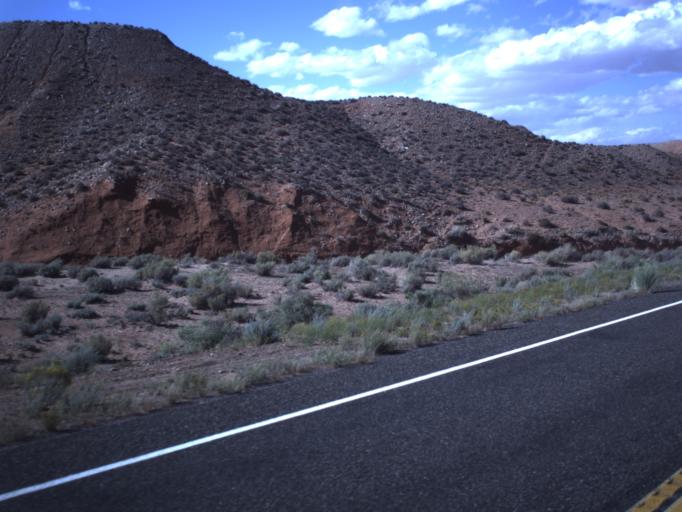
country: US
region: Utah
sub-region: Wayne County
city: Loa
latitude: 38.1380
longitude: -110.6095
